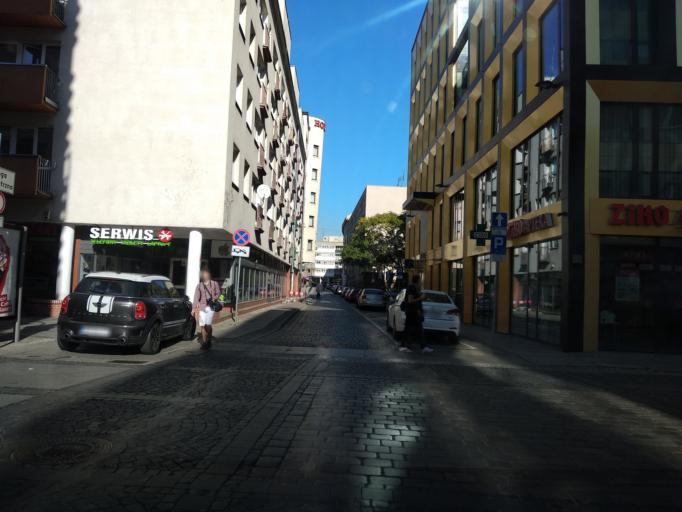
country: PL
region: Lower Silesian Voivodeship
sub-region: Powiat wroclawski
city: Wroclaw
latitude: 51.1085
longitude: 17.0352
